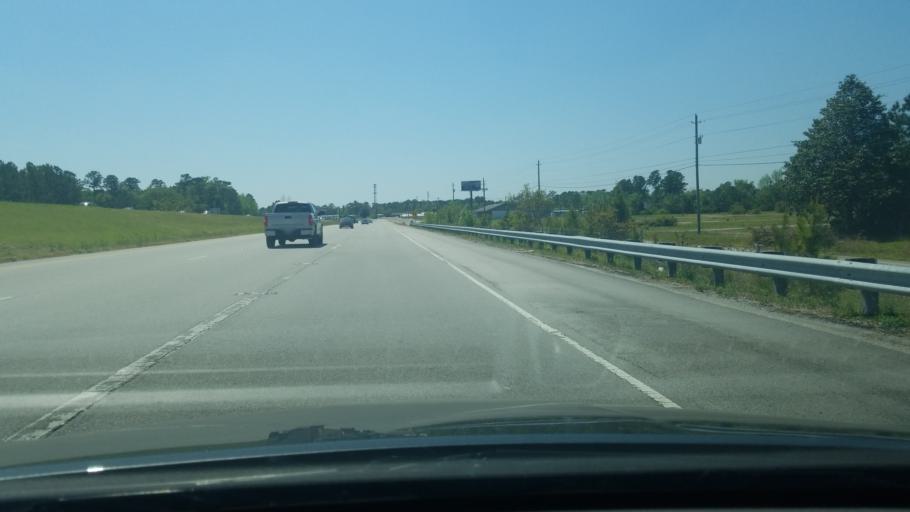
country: US
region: North Carolina
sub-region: Onslow County
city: Jacksonville
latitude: 34.7401
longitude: -77.4611
